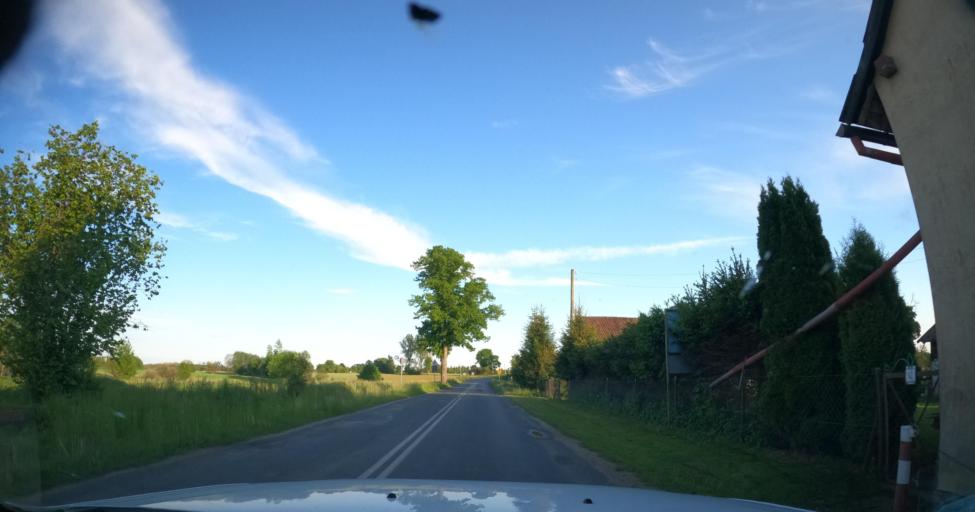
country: PL
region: Warmian-Masurian Voivodeship
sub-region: Powiat lidzbarski
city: Orneta
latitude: 54.1762
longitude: 20.1588
